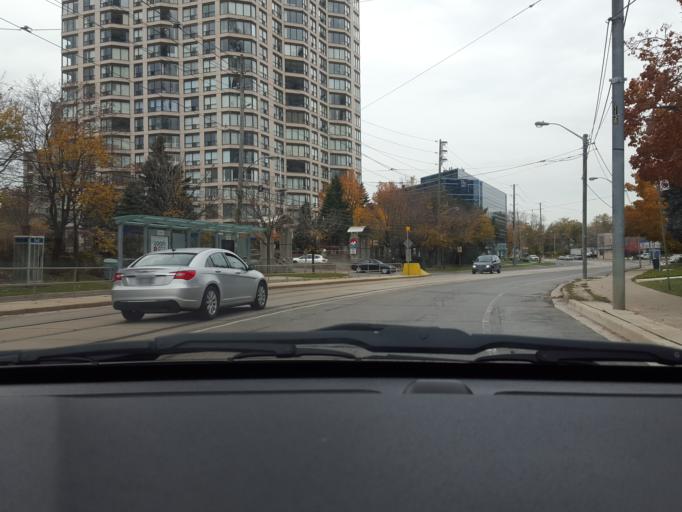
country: CA
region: Ontario
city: Etobicoke
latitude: 43.6206
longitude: -79.4834
